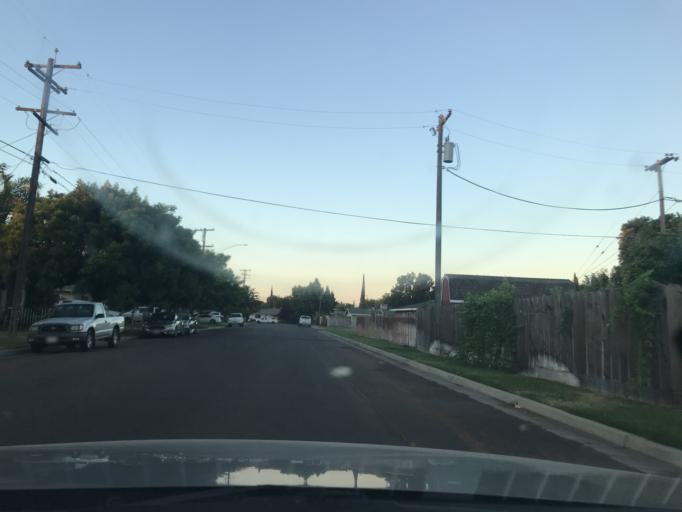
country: US
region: California
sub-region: Merced County
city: Atwater
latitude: 37.3584
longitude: -120.5936
